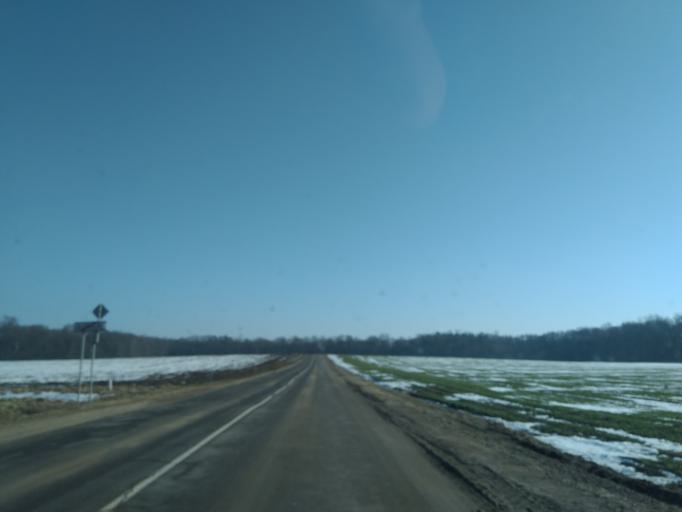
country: BY
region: Minsk
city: Nyasvizh
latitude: 53.2028
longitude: 26.6484
